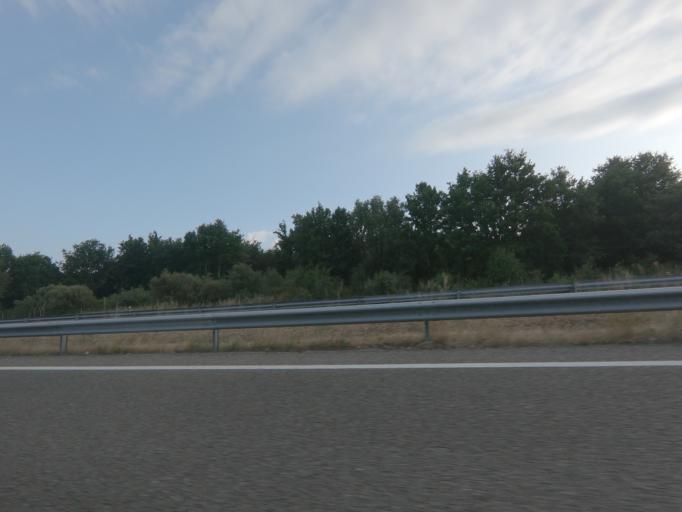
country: ES
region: Galicia
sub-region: Provincia de Ourense
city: Allariz
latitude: 42.1988
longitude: -7.7823
